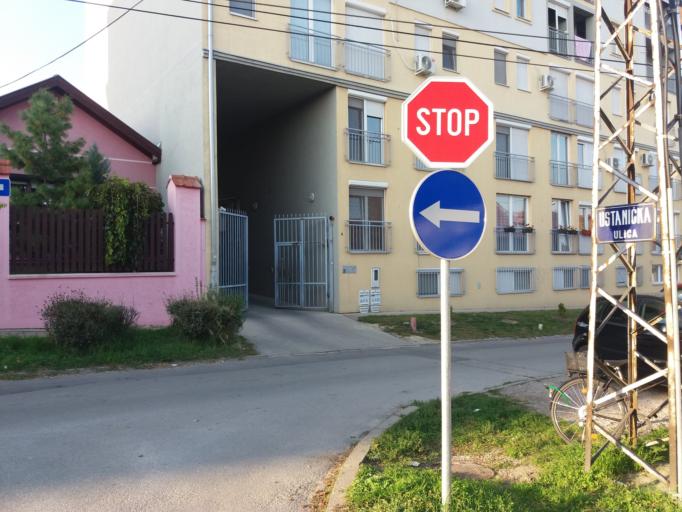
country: RS
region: Autonomna Pokrajina Vojvodina
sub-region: Severnobacki Okrug
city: Subotica
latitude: 46.0941
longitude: 19.6638
